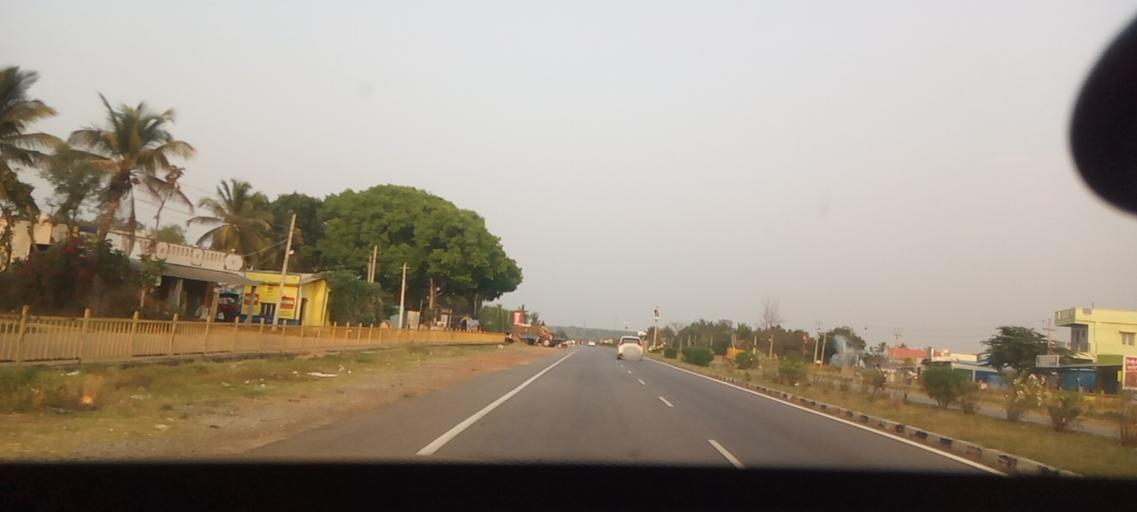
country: IN
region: Karnataka
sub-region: Tumkur
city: Kunigal
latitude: 12.9933
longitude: 76.8943
